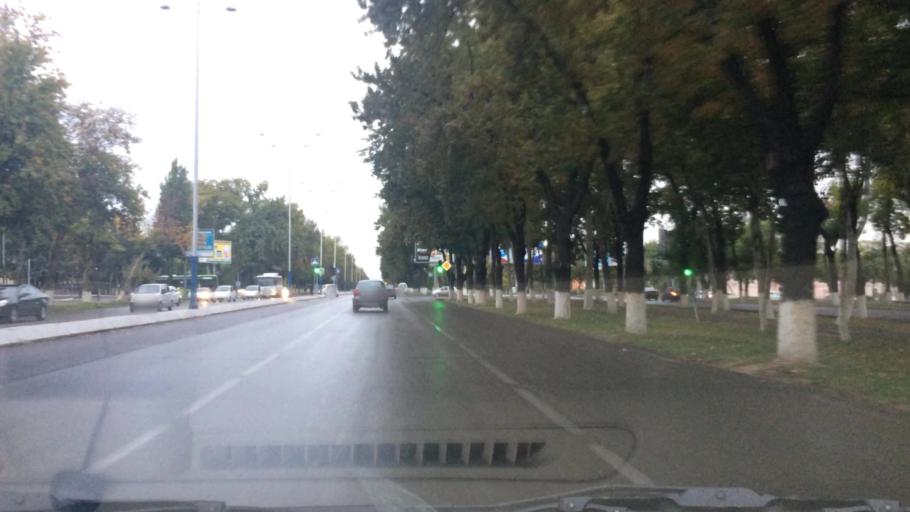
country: UZ
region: Toshkent Shahri
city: Tashkent
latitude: 41.2694
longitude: 69.2016
